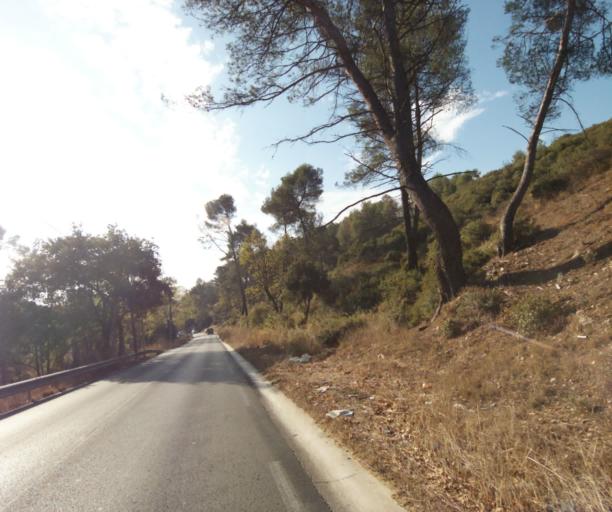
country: FR
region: Provence-Alpes-Cote d'Azur
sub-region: Departement des Bouches-du-Rhone
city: Allauch
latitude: 43.3121
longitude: 5.4997
